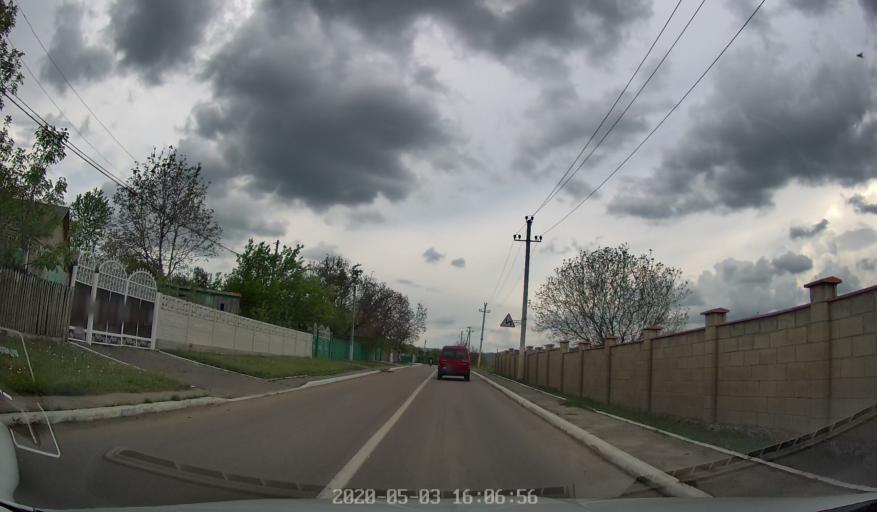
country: MD
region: Calarasi
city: Calarasi
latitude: 47.1957
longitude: 28.3496
